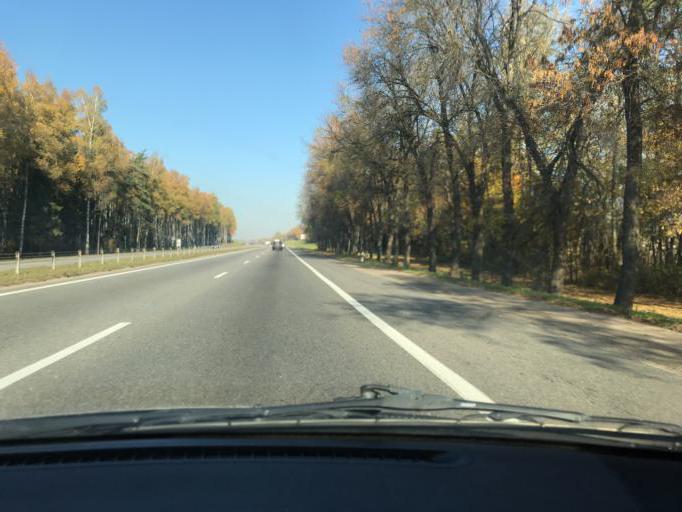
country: BY
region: Minsk
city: Samakhvalavichy
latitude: 53.7611
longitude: 27.5186
